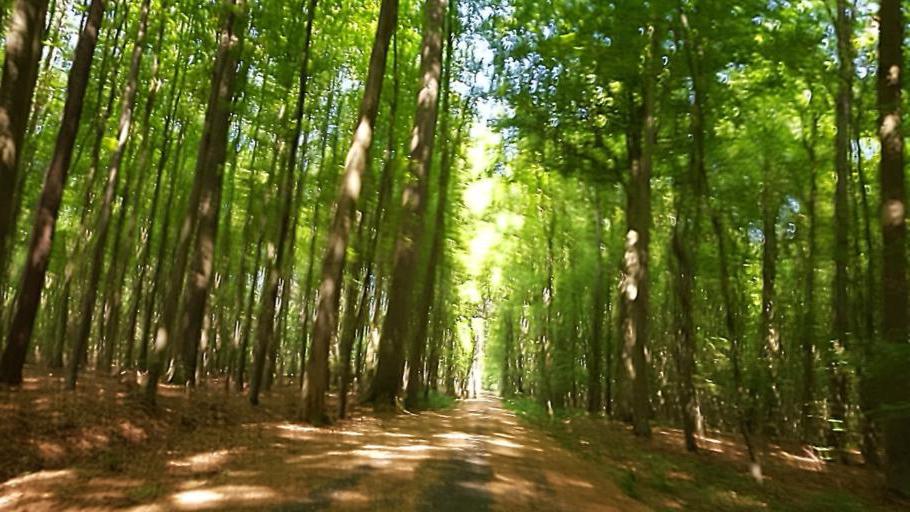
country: BE
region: Flanders
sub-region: Provincie Vlaams-Brabant
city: Tervuren
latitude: 50.8117
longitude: 4.5249
